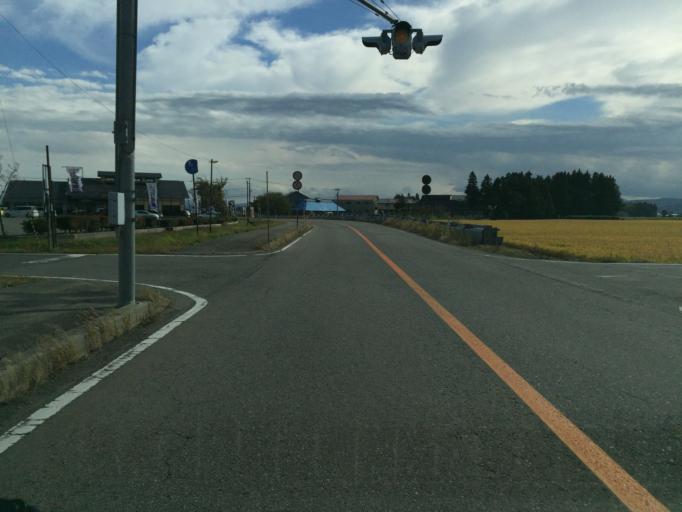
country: JP
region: Fukushima
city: Inawashiro
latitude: 37.5454
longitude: 140.0777
